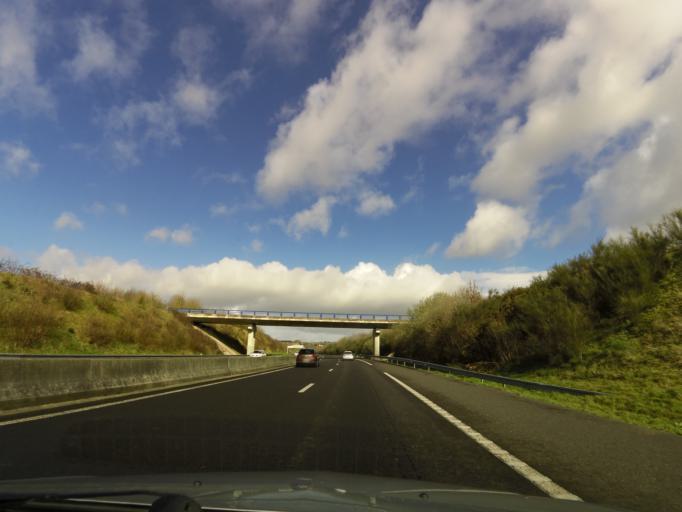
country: FR
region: Lower Normandy
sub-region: Departement de la Manche
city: Conde-sur-Vire
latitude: 49.0629
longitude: -1.0129
